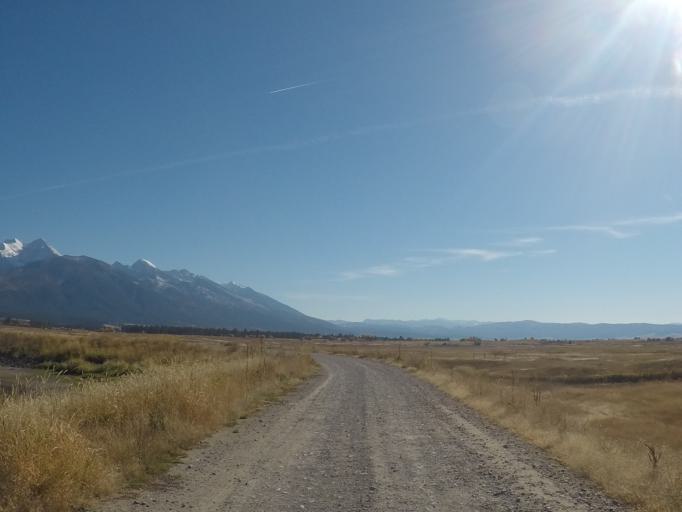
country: US
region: Montana
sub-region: Lake County
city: Ronan
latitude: 47.4542
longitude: -114.0835
